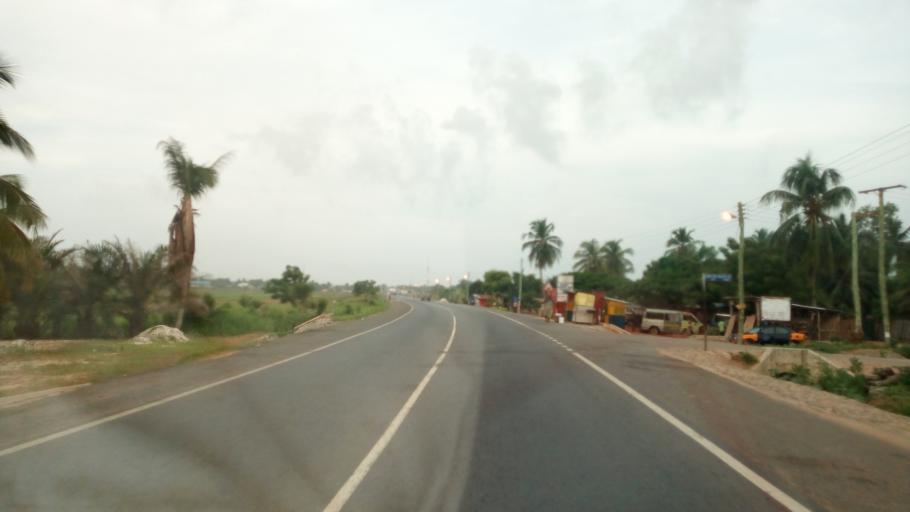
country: GH
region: Volta
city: Keta
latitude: 6.0794
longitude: 1.0461
